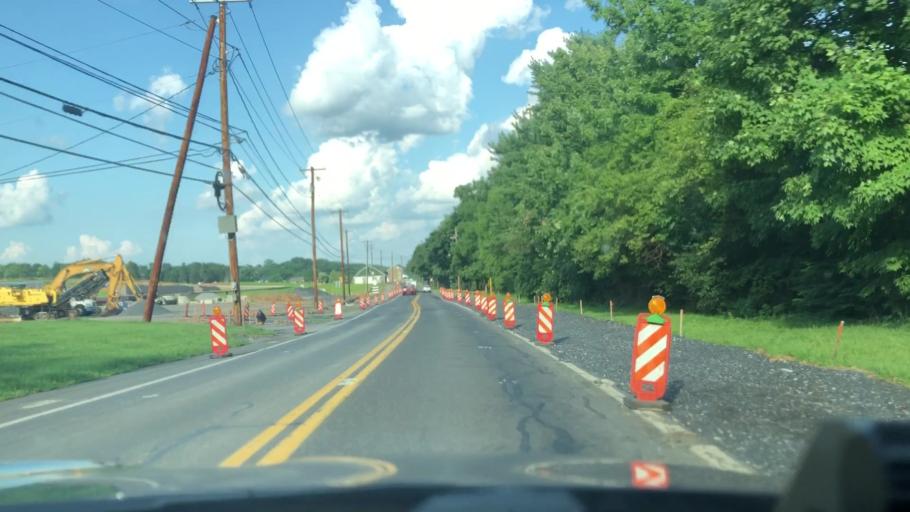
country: US
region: Pennsylvania
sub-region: Lehigh County
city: Wescosville
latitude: 40.6125
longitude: -75.5571
